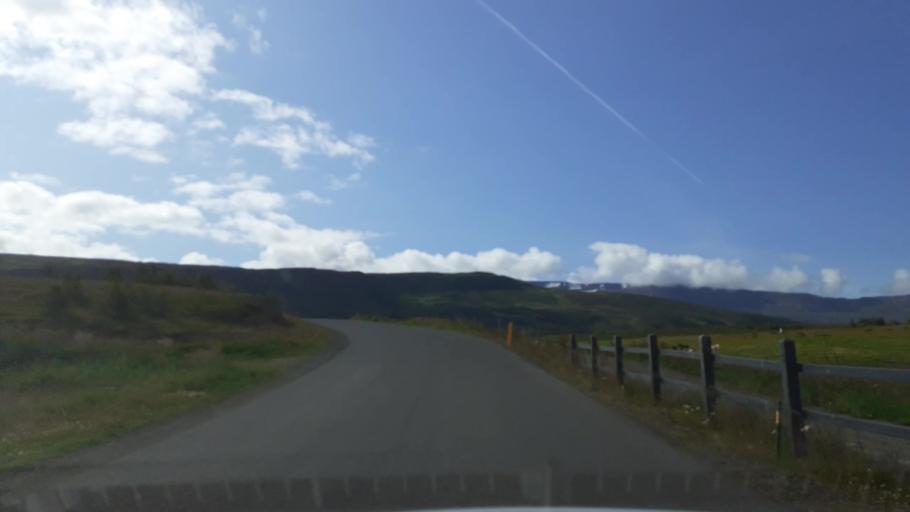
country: IS
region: Northeast
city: Akureyri
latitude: 65.6512
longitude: -18.0936
